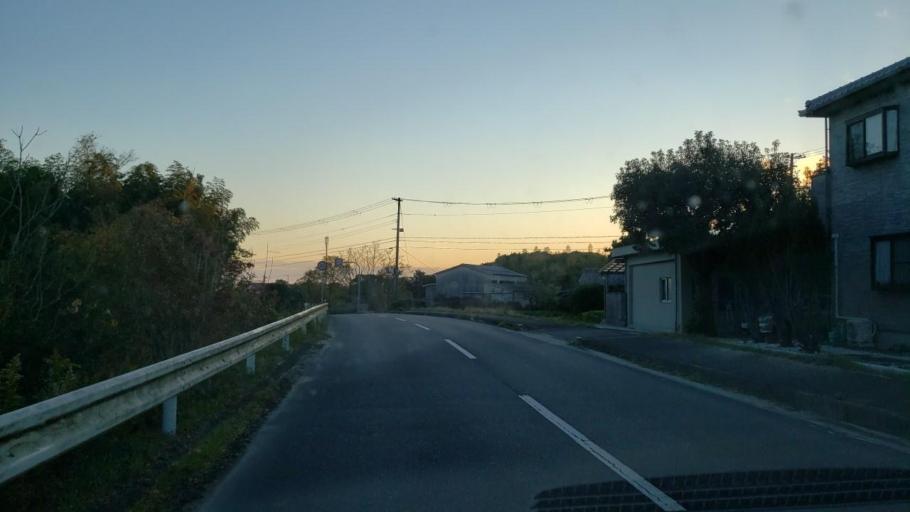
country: JP
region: Hyogo
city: Sumoto
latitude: 34.3527
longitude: 134.7839
